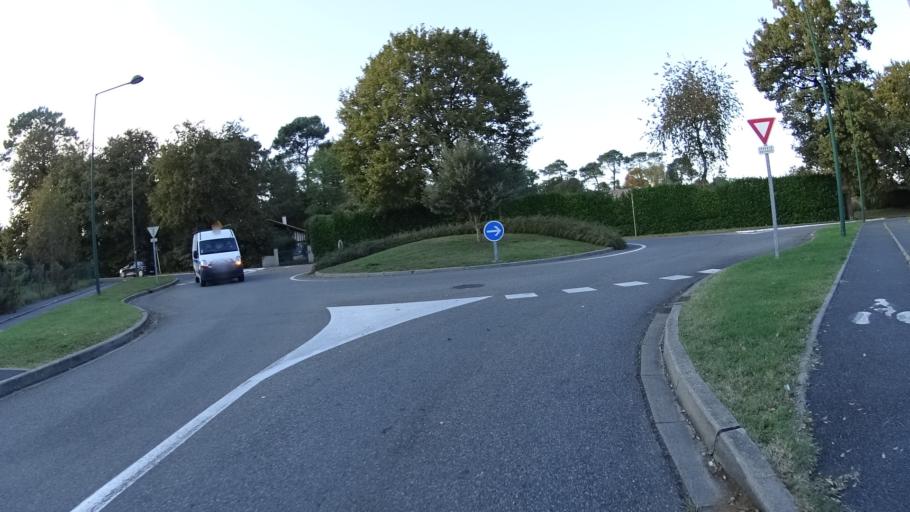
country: FR
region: Aquitaine
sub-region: Departement des Landes
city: Saint-Paul-les-Dax
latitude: 43.7371
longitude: -1.0483
